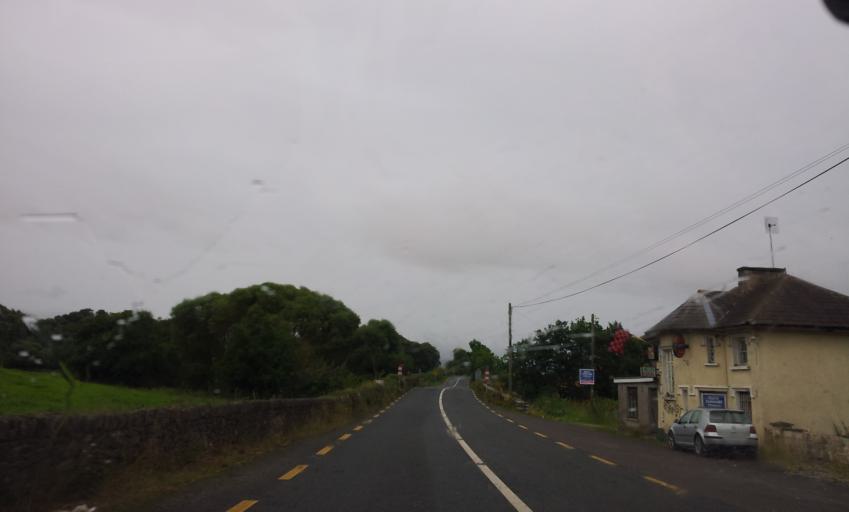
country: IE
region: Munster
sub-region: County Cork
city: Mallow
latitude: 52.2203
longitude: -8.5033
